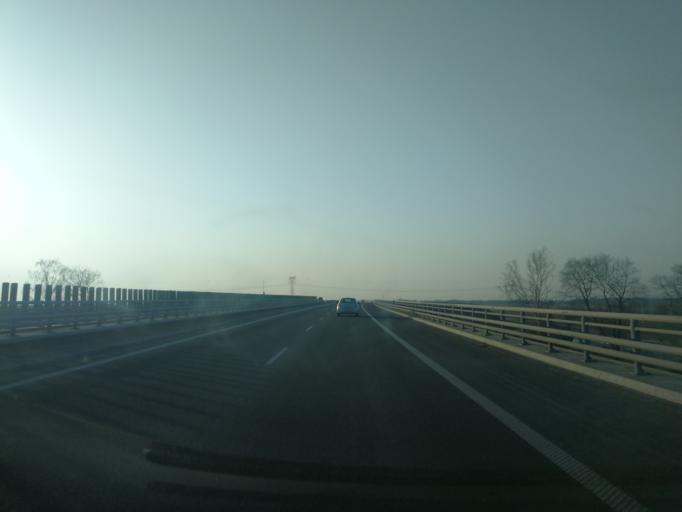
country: PL
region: Warmian-Masurian Voivodeship
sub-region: Powiat elblaski
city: Gronowo Elblaskie
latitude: 54.1657
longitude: 19.2411
